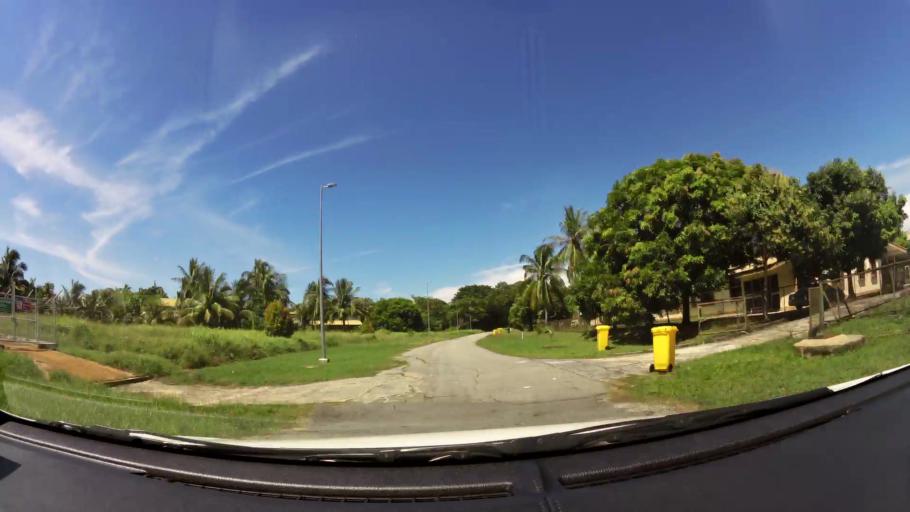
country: BN
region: Brunei and Muara
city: Bandar Seri Begawan
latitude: 5.0341
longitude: 115.0688
